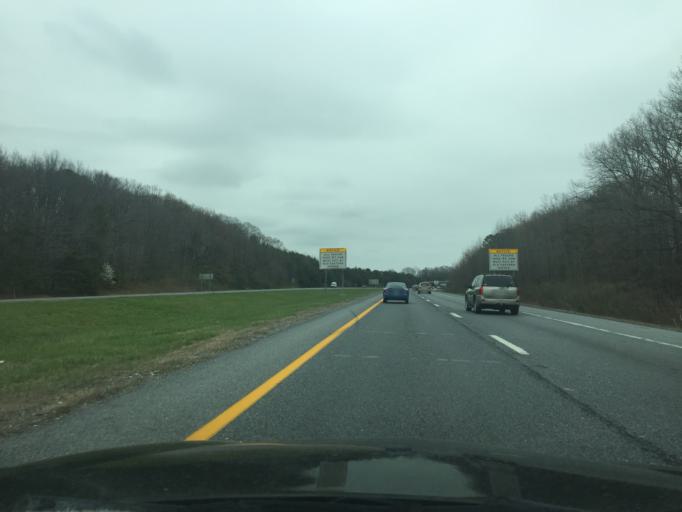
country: US
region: Maryland
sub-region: Baltimore County
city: Essex
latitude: 39.3223
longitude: -76.4699
